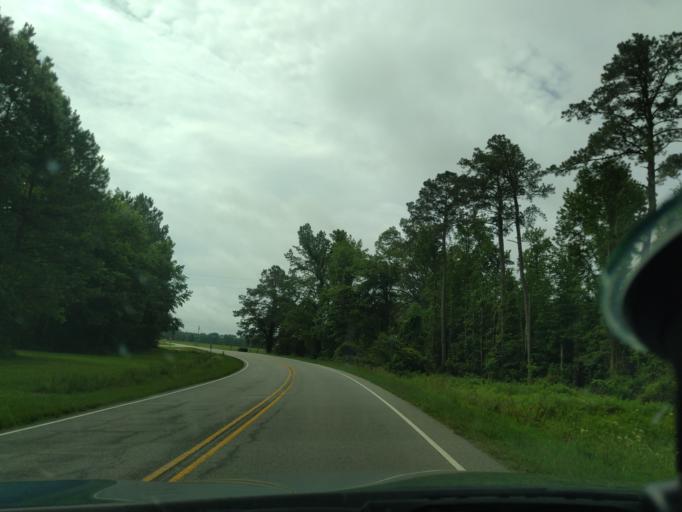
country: US
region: North Carolina
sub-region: Washington County
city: Plymouth
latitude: 35.8965
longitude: -76.6096
